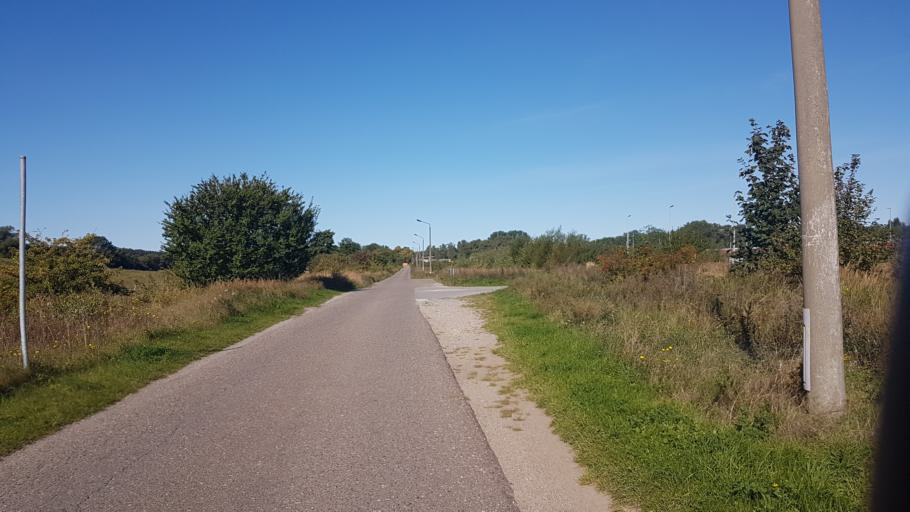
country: DE
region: Mecklenburg-Vorpommern
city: Sagard
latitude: 54.4988
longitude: 13.5431
